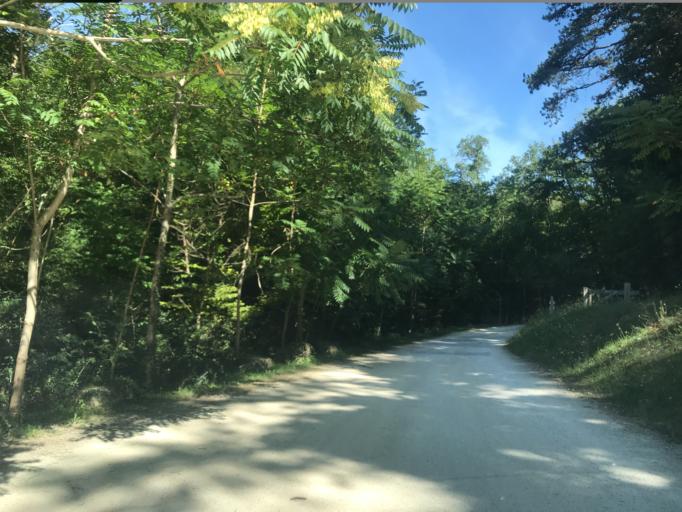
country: FR
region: Aquitaine
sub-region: Departement de la Dordogne
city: Sarlat-la-Caneda
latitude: 44.9106
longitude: 1.1405
